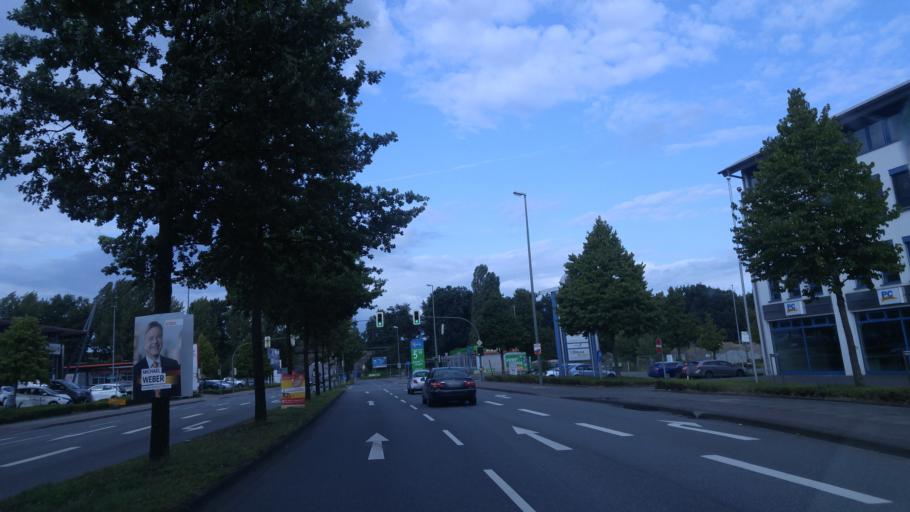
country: DE
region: North Rhine-Westphalia
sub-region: Regierungsbezirk Detmold
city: Bielefeld
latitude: 52.0307
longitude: 8.5441
